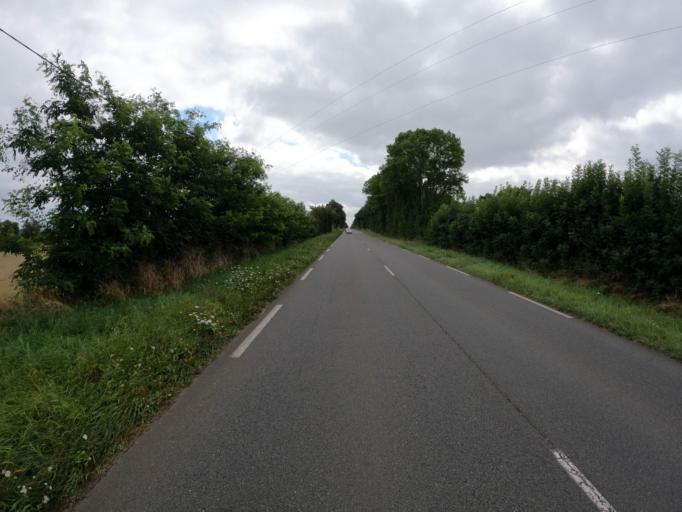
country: FR
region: Poitou-Charentes
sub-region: Departement de la Charente
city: Exideuil
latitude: 45.9522
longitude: 0.7126
